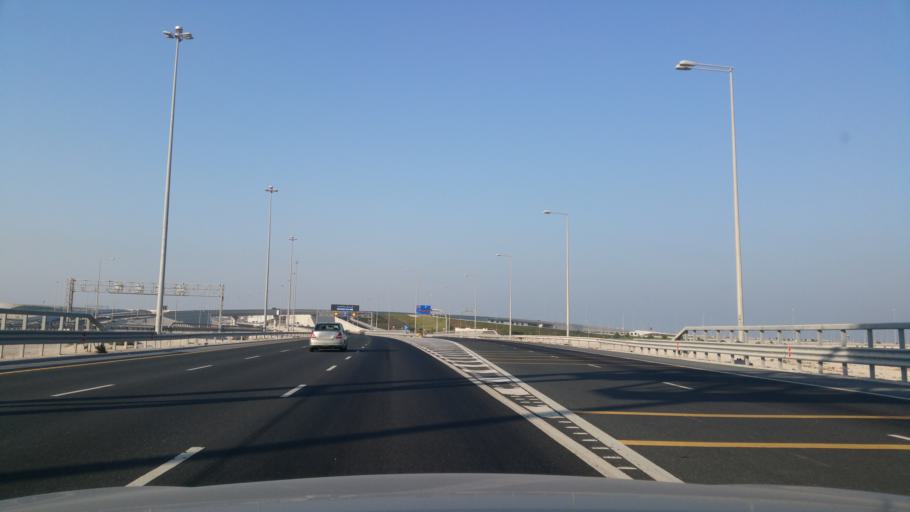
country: QA
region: Al Wakrah
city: Al Wakrah
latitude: 25.1172
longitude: 51.5869
